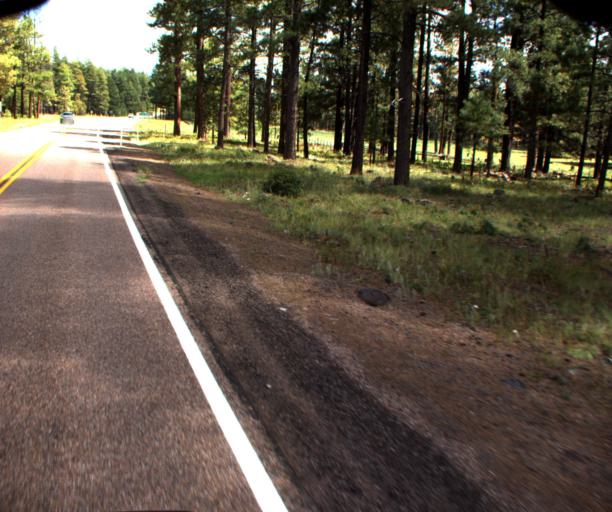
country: US
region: Arizona
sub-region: Navajo County
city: Pinetop-Lakeside
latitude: 34.0528
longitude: -109.7330
